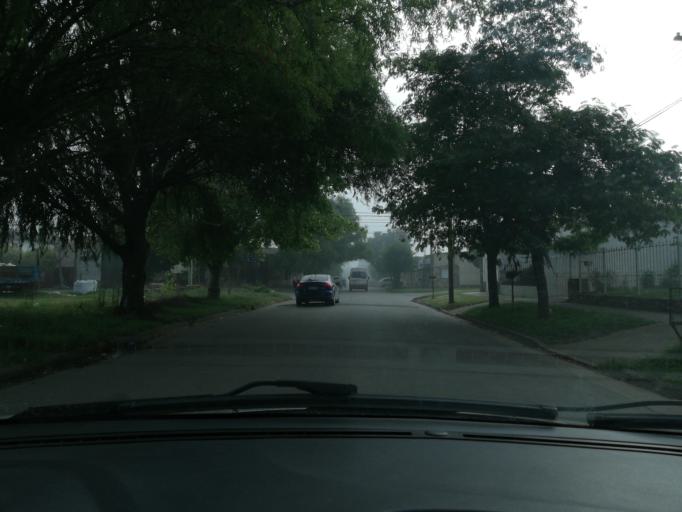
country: AR
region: Buenos Aires
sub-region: Partido de Balcarce
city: Balcarce
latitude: -37.8429
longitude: -58.2490
